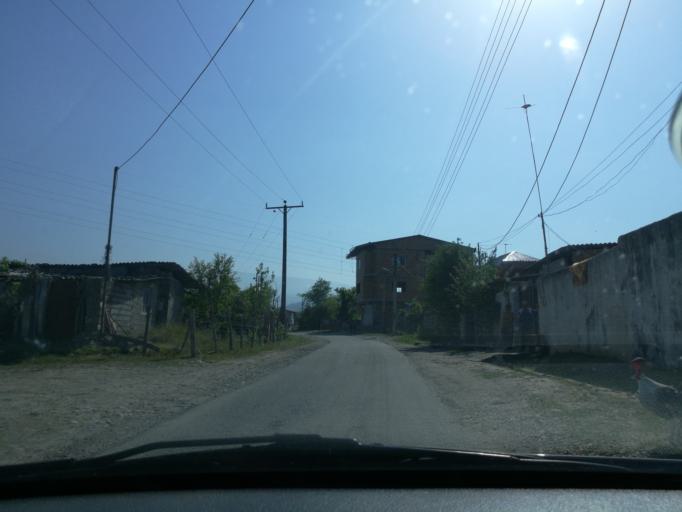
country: IR
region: Mazandaran
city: Chalus
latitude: 36.6610
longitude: 51.4373
